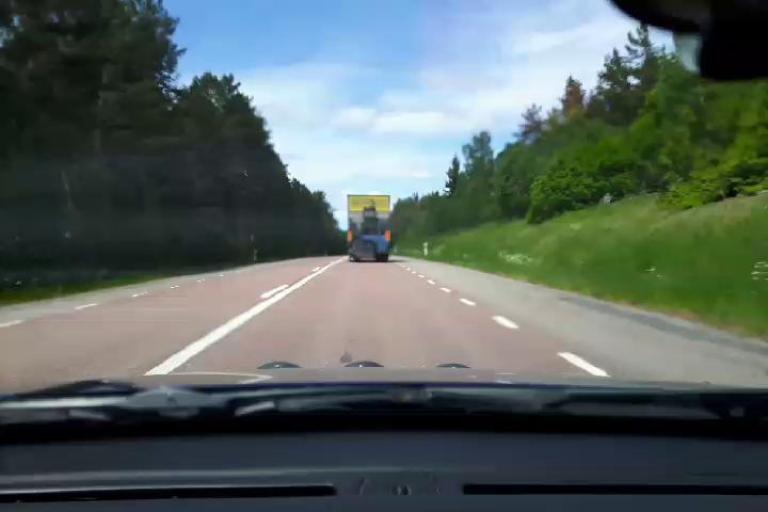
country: SE
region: Uppsala
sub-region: Osthammars Kommun
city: Bjorklinge
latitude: 60.1379
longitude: 17.5059
